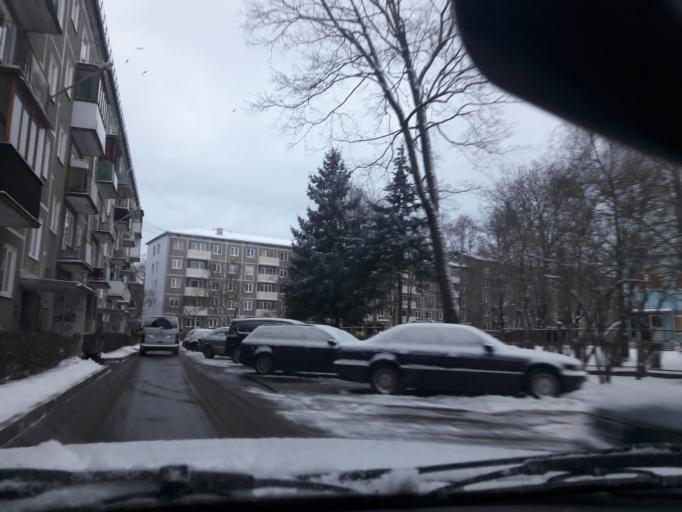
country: LV
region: Kekava
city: Balozi
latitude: 56.9111
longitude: 24.1739
